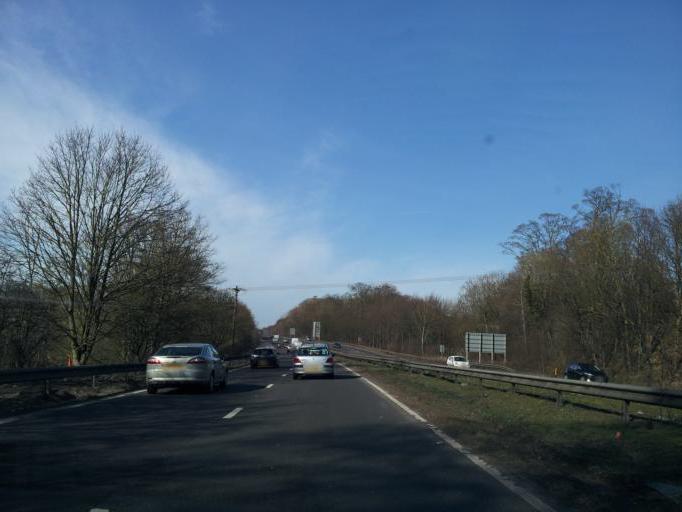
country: GB
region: England
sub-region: Lincolnshire
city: Grantham
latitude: 52.8174
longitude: -0.6232
